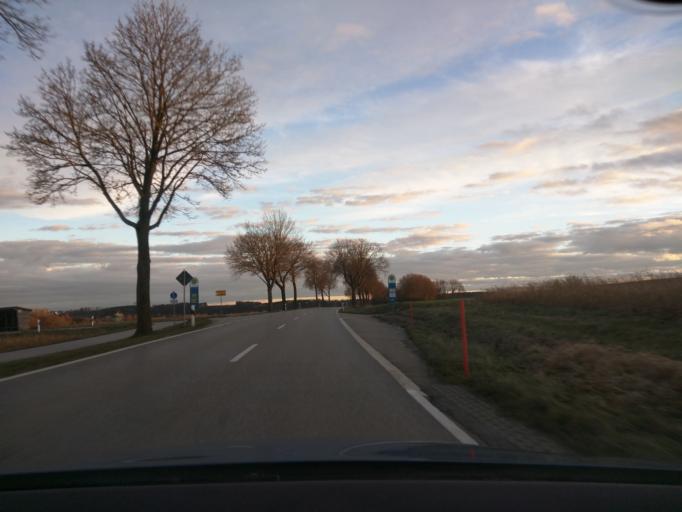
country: DE
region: Bavaria
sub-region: Upper Bavaria
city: Zolling
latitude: 48.4619
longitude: 11.7676
